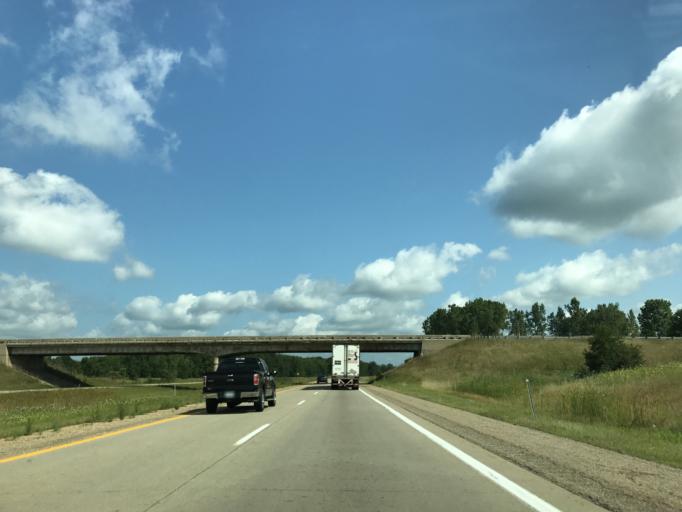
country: US
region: Michigan
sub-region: Branch County
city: Coldwater
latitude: 41.8970
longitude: -84.9906
